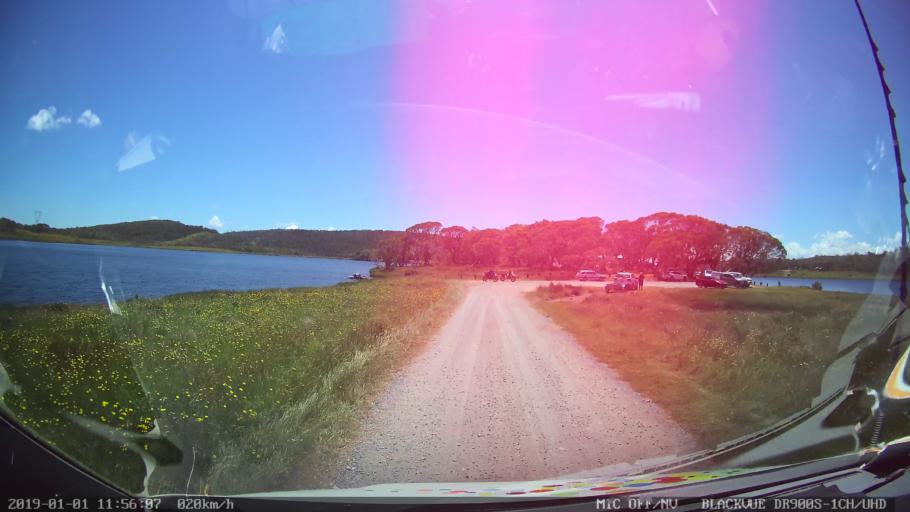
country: AU
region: New South Wales
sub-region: Snowy River
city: Jindabyne
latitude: -35.8866
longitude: 148.4502
